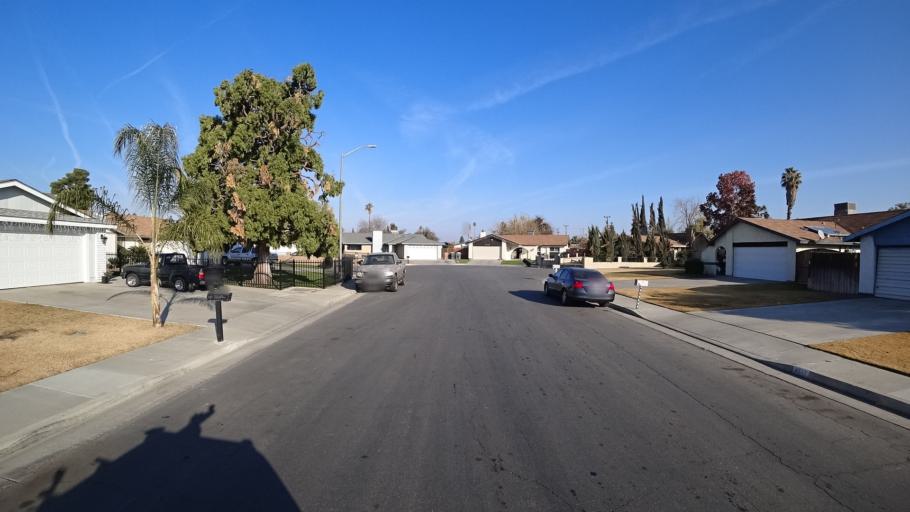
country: US
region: California
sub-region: Kern County
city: Greenfield
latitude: 35.3133
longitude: -119.0084
